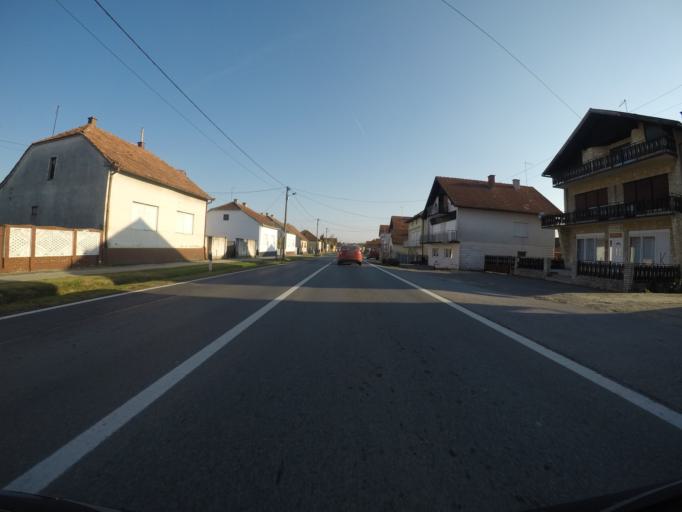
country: HR
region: Virovitick-Podravska
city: Pitomaca
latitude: 45.9610
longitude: 17.2227
